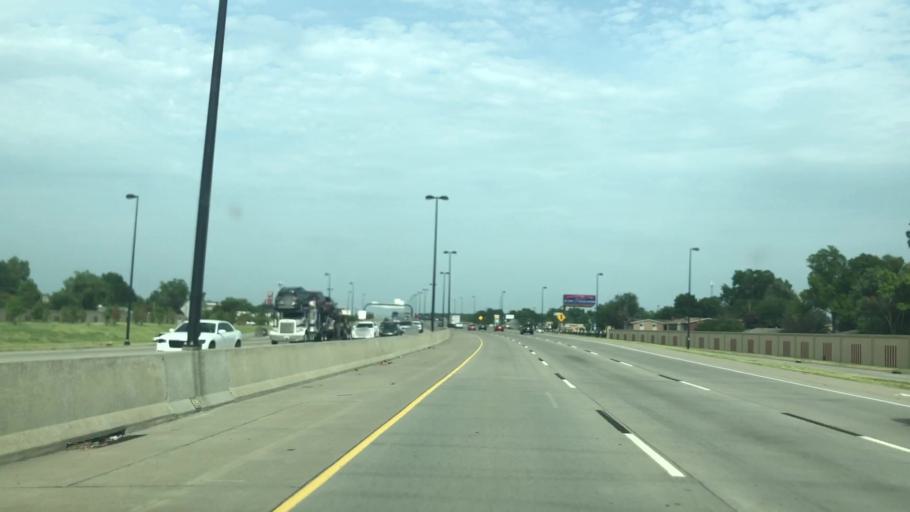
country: US
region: Oklahoma
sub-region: Tulsa County
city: Tulsa
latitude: 36.0897
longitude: -95.9815
